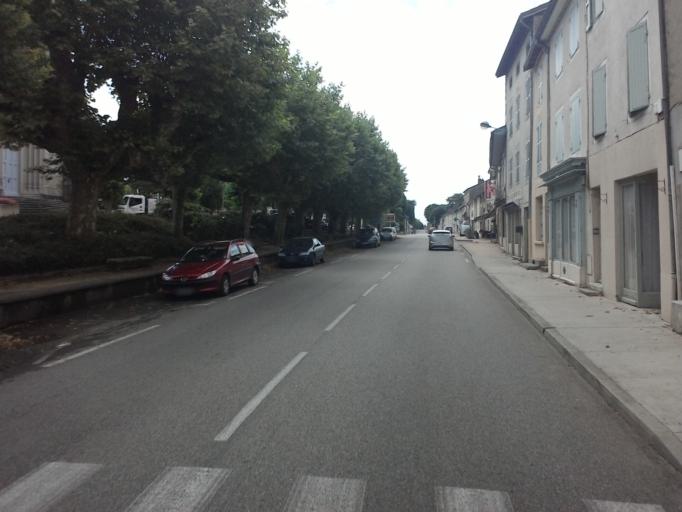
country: FR
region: Rhone-Alpes
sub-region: Departement de l'Ain
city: Coligny
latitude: 46.3842
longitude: 5.3458
